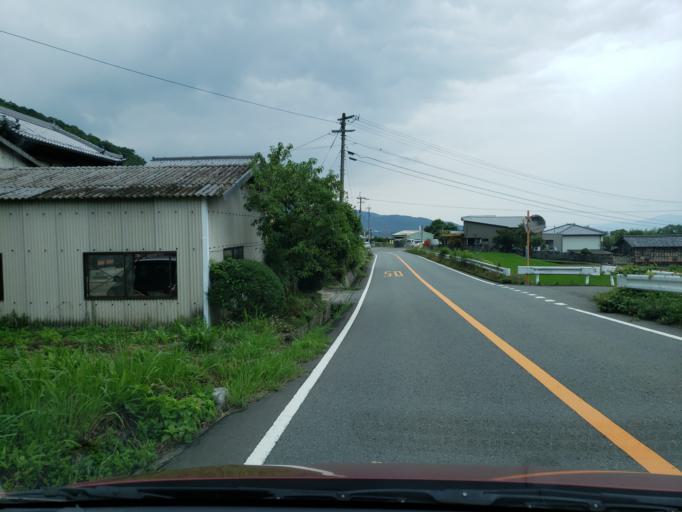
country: JP
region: Tokushima
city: Kamojimacho-jogejima
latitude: 34.1053
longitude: 134.2508
